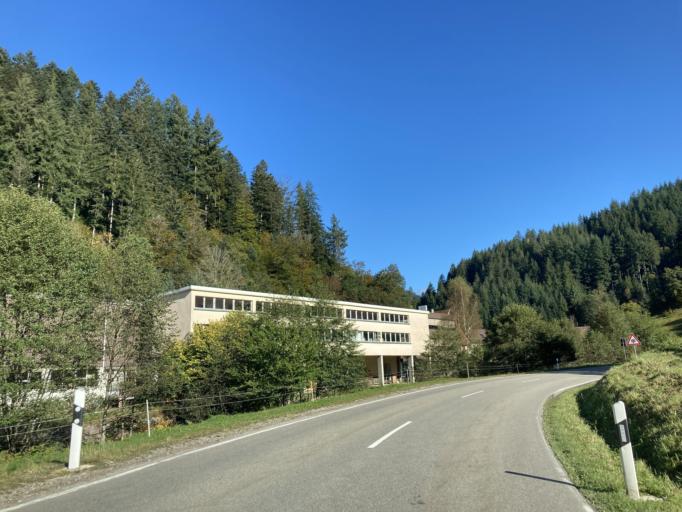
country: DE
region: Baden-Wuerttemberg
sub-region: Karlsruhe Region
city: Bad Rippoldsau-Schapbach
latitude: 48.3960
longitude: 8.3109
